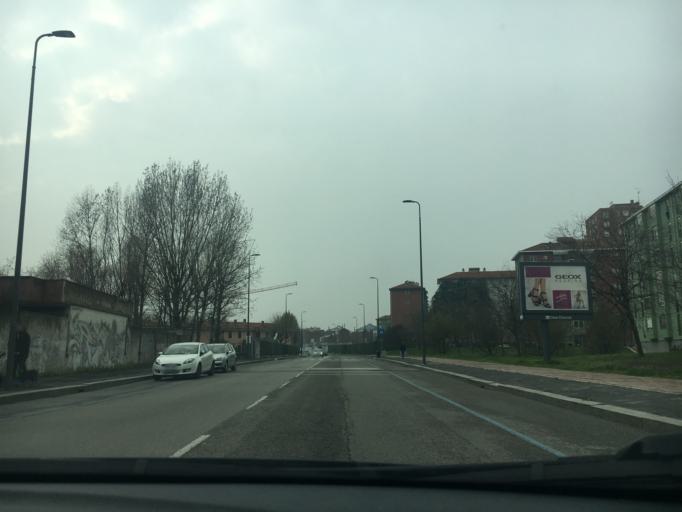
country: IT
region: Lombardy
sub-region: Citta metropolitana di Milano
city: Pero
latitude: 45.4912
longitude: 9.1117
